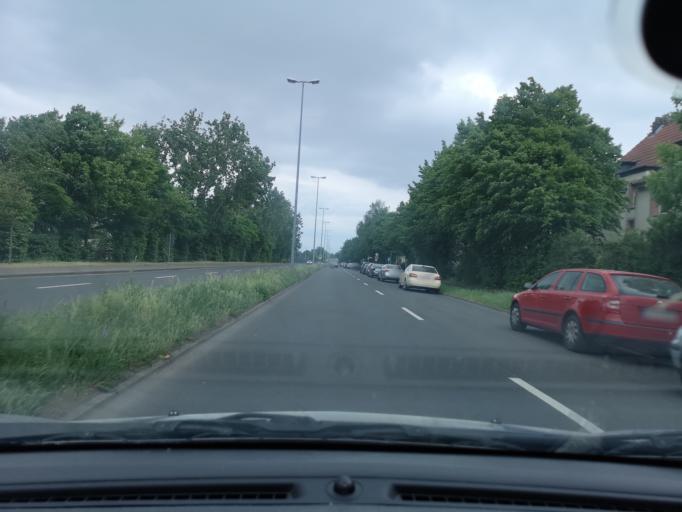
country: DE
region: Lower Saxony
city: Garbsen-Mitte
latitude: 52.4158
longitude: 9.6724
